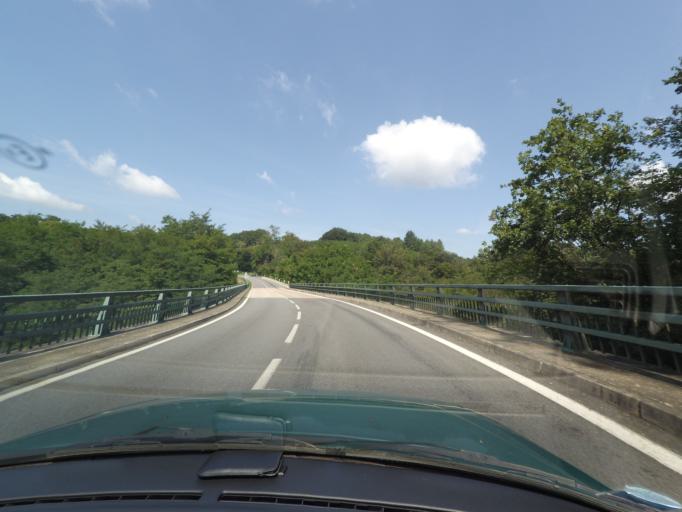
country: FR
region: Limousin
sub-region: Departement de la Haute-Vienne
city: Linards
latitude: 45.7669
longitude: 1.5551
